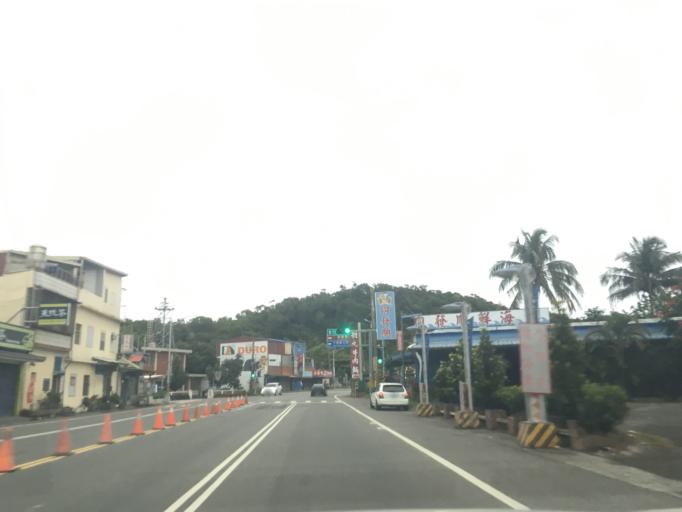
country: TW
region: Taiwan
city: Hengchun
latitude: 22.3397
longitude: 120.8932
